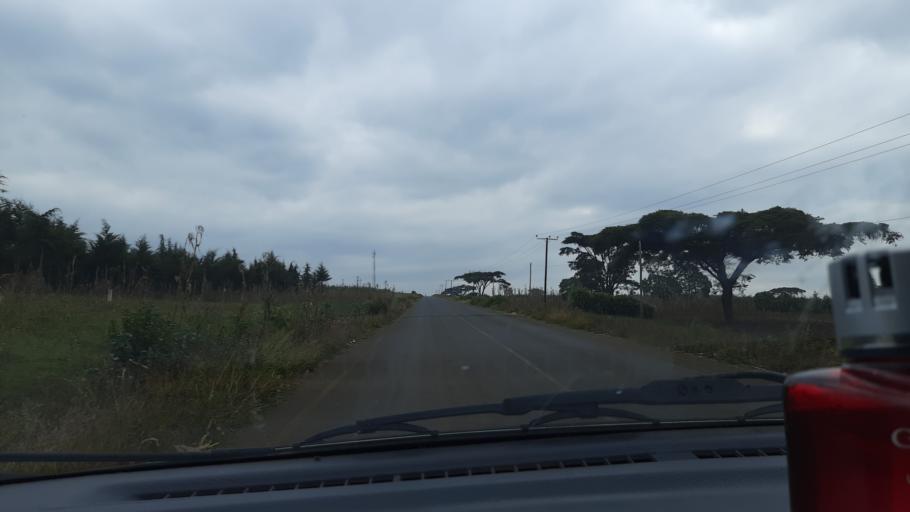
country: TZ
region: Kilimanjaro
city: Moshi
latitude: -2.9486
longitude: 37.5007
